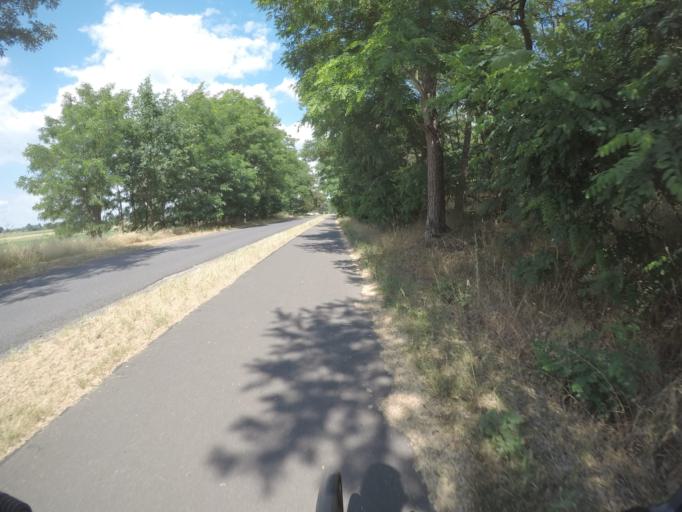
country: DE
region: Brandenburg
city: Roskow
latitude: 52.4344
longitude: 12.7096
